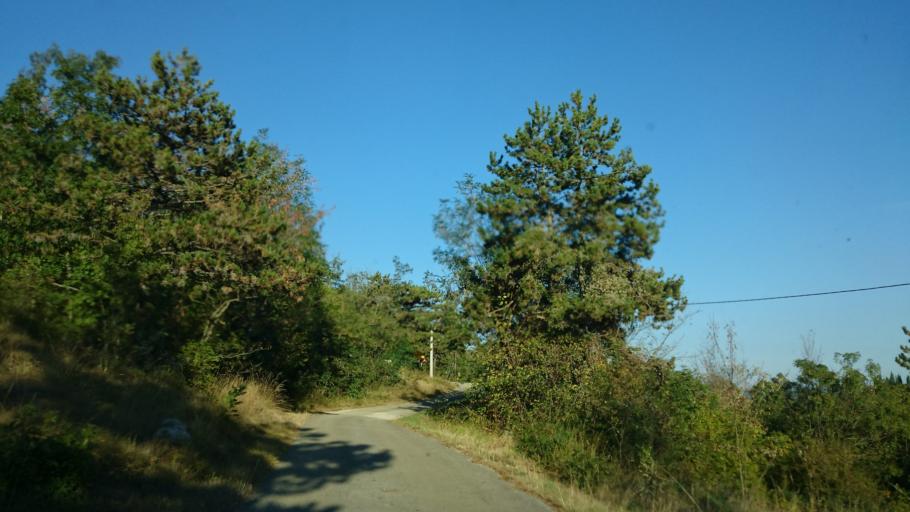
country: HR
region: Istarska
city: Karojba
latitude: 45.3898
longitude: 13.8169
